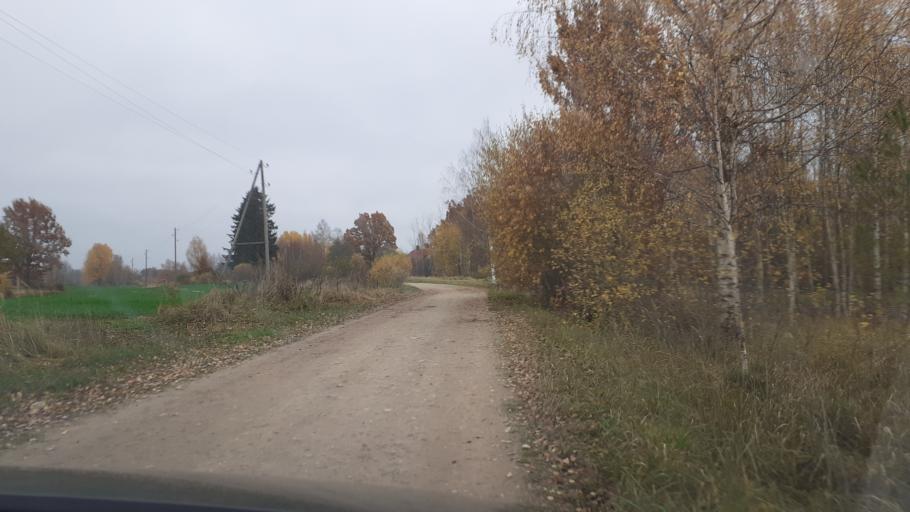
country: LV
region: Saldus Rajons
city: Saldus
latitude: 56.8637
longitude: 22.3200
